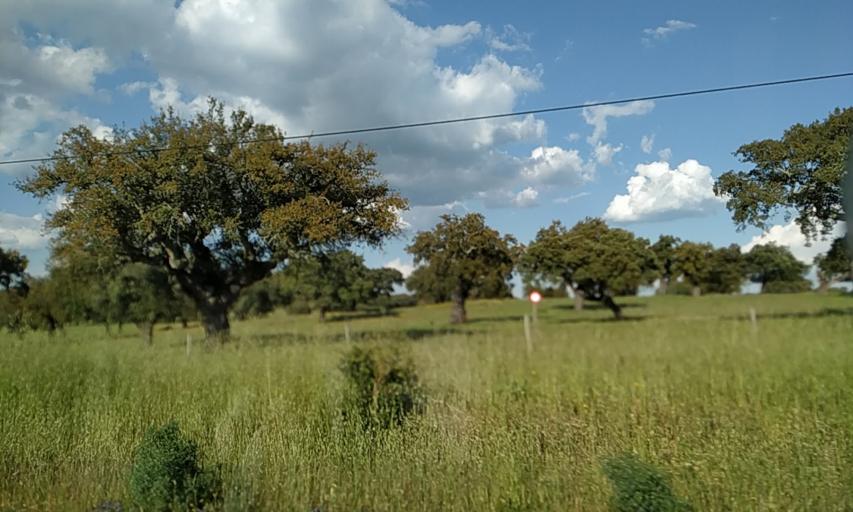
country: PT
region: Portalegre
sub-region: Portalegre
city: Urra
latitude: 39.1740
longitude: -7.4537
